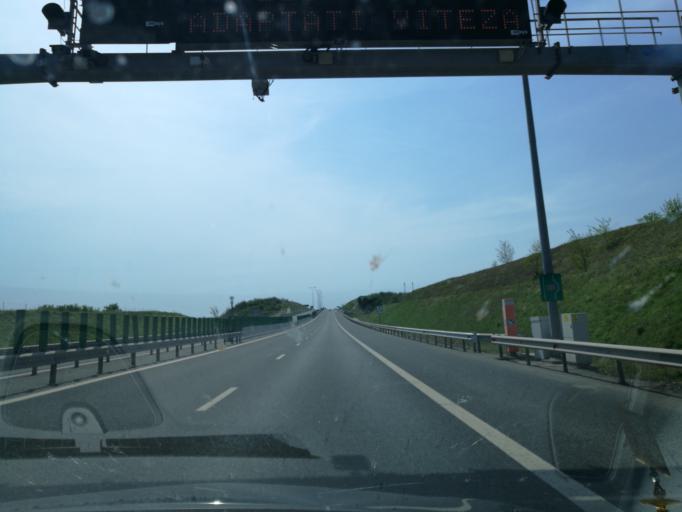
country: RO
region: Constanta
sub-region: Oras Cernavoda
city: Cernavoda
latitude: 44.3250
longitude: 28.0302
